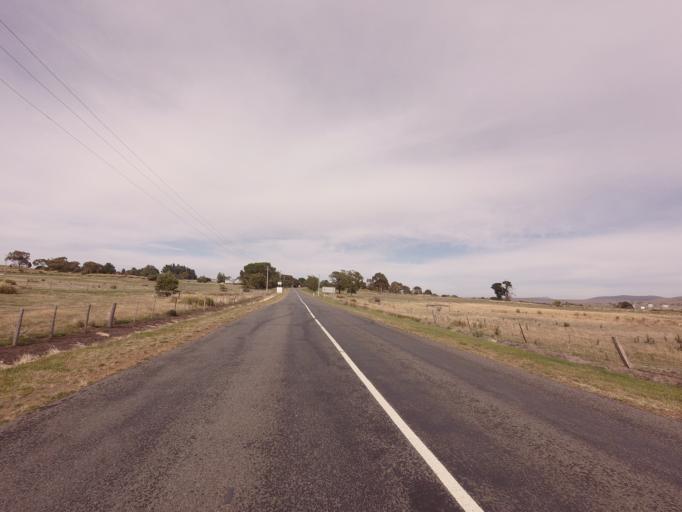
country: AU
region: Tasmania
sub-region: Brighton
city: Bridgewater
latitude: -42.2955
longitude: 147.3851
